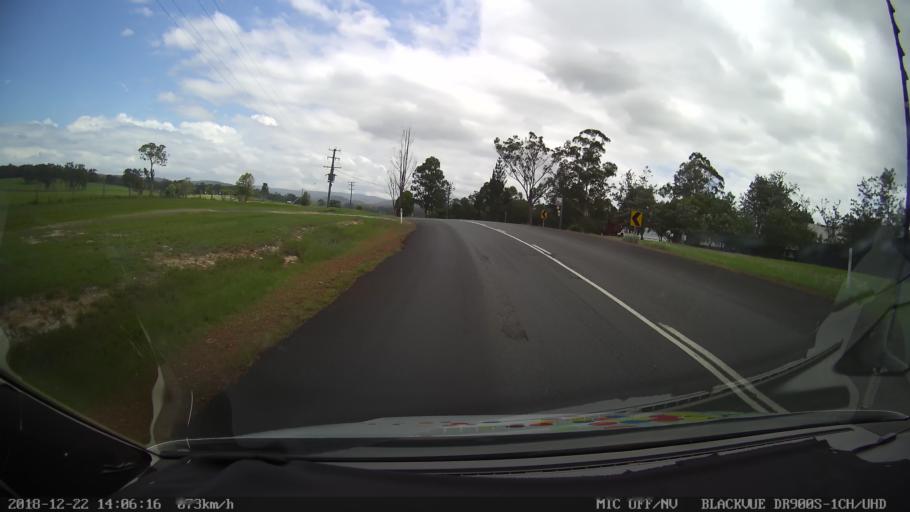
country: AU
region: New South Wales
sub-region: Clarence Valley
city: Coutts Crossing
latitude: -29.9537
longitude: 152.7276
